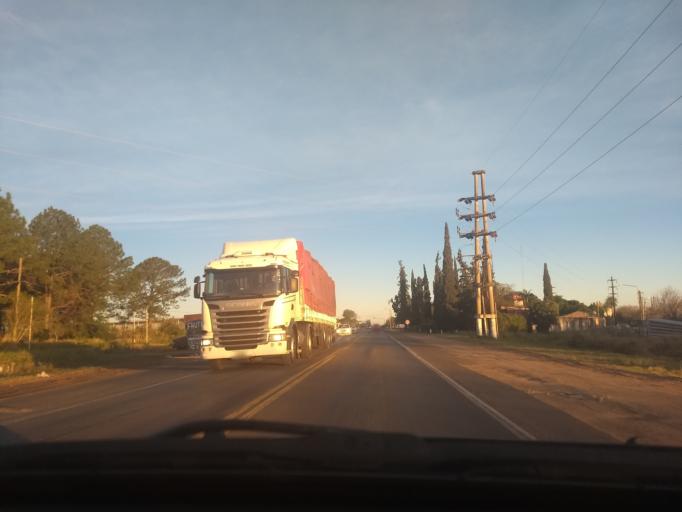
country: AR
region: Corrientes
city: Corrientes
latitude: -27.4878
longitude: -58.7808
